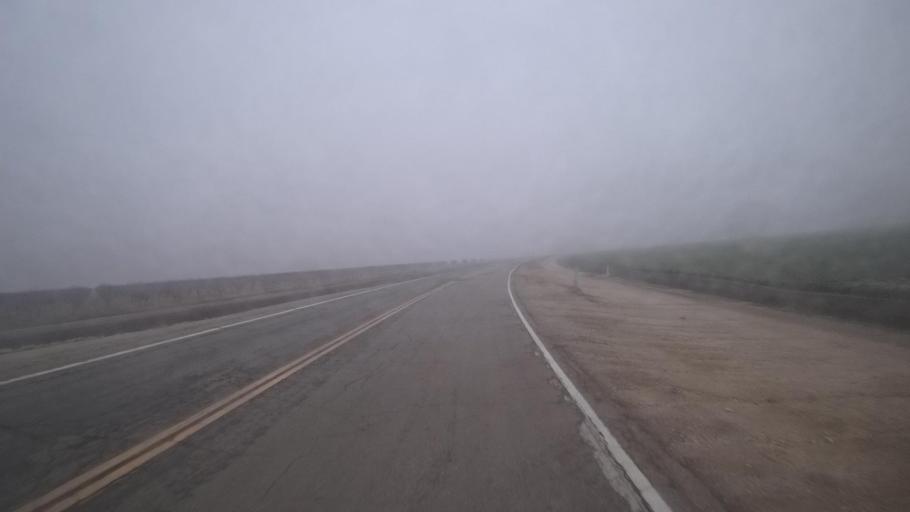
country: US
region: California
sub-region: Kern County
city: Buttonwillow
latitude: 35.4336
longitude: -119.5425
